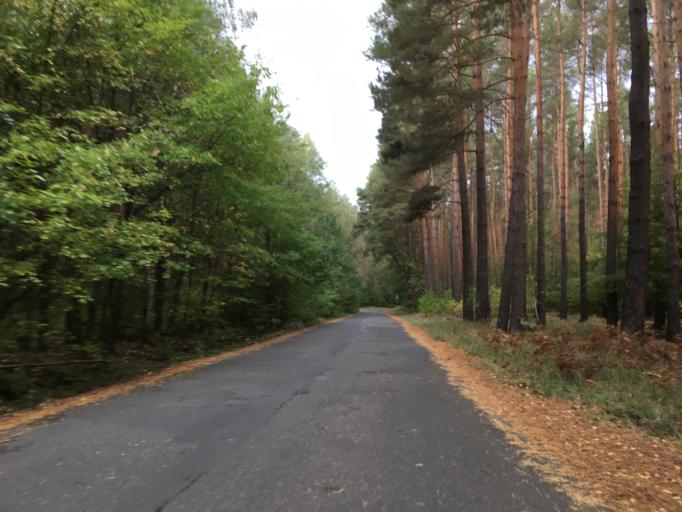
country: DE
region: Brandenburg
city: Birkenwerder
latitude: 52.6958
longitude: 13.3105
